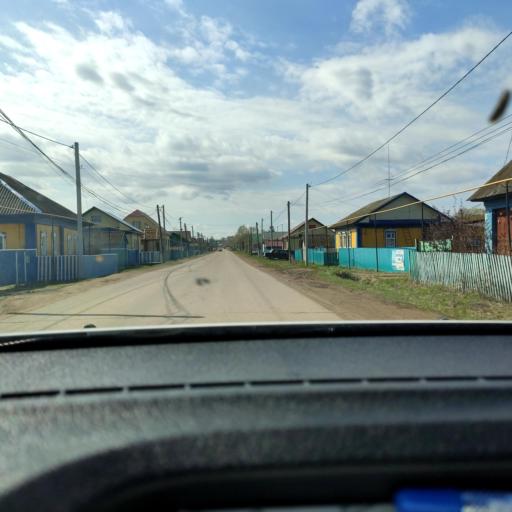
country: RU
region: Bashkortostan
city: Starobaltachevo
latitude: 56.0002
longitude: 55.9309
